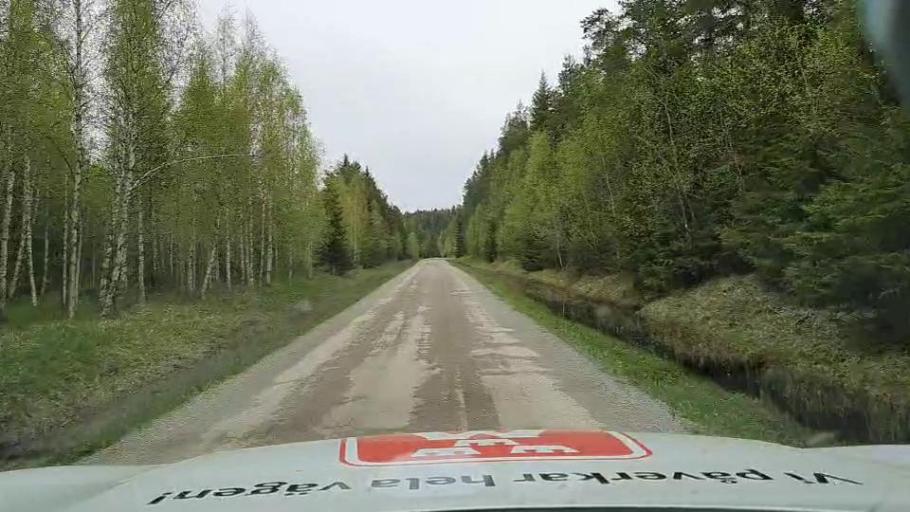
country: SE
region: Jaemtland
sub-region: OEstersunds Kommun
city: Brunflo
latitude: 62.9406
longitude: 14.6655
